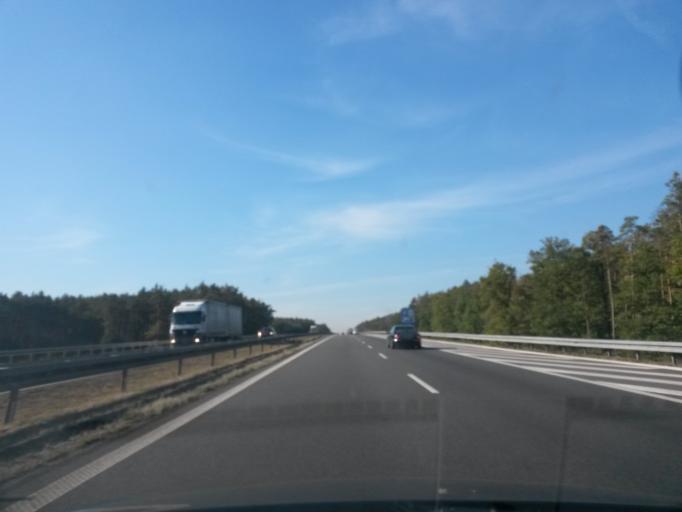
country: PL
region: Opole Voivodeship
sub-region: Powiat opolski
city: Komprachcice
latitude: 50.6150
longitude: 17.7706
